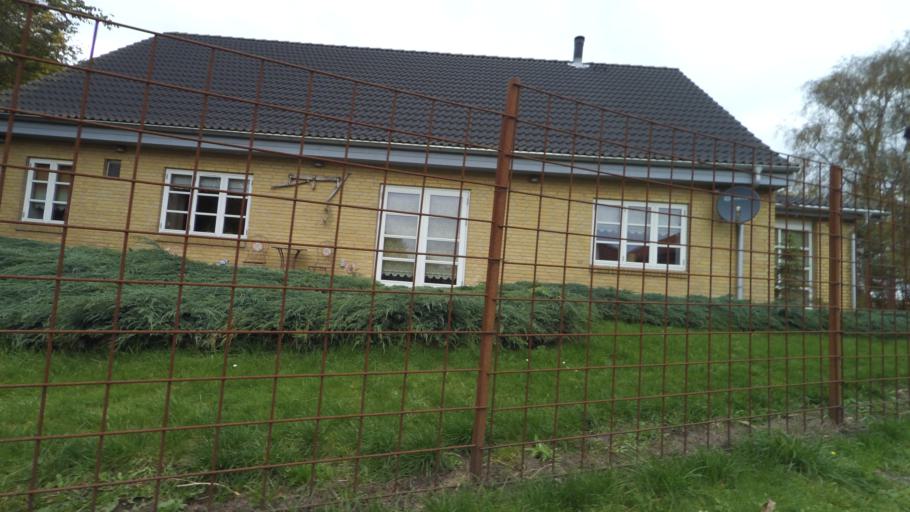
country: DK
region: Central Jutland
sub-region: Arhus Kommune
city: Kolt
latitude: 56.1467
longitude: 10.0585
